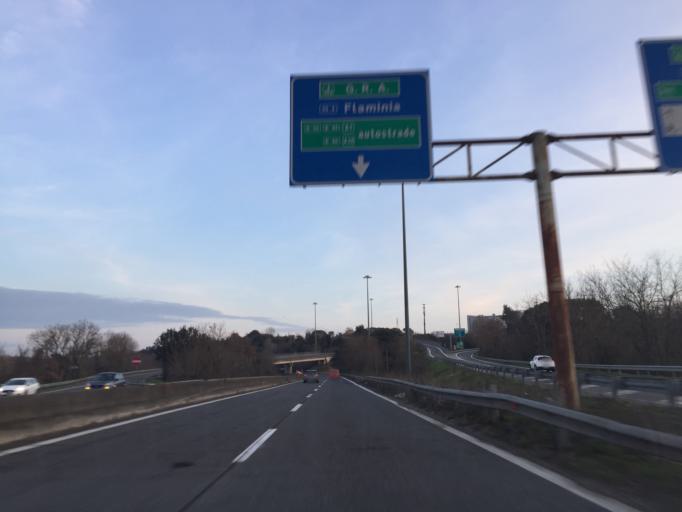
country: IT
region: Latium
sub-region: Citta metropolitana di Roma Capitale
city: Monte Caminetto
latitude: 41.9911
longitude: 12.4687
